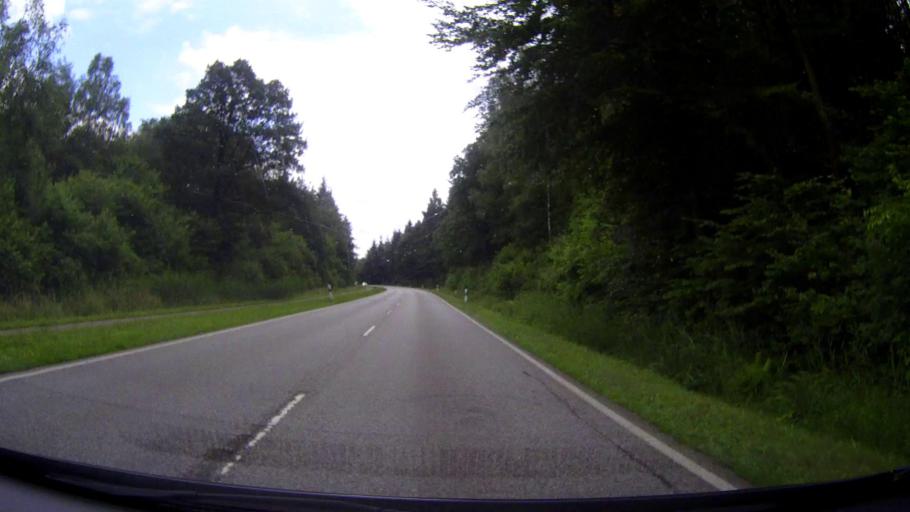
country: DE
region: Schleswig-Holstein
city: Meezen
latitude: 54.0711
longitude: 9.7312
